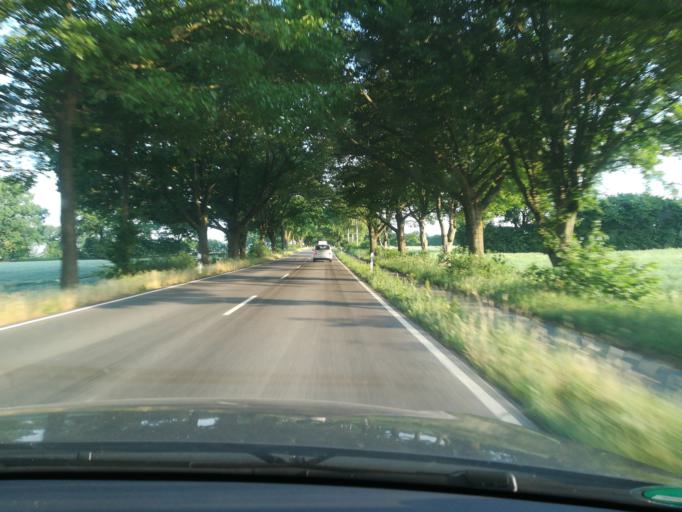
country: DE
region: Schleswig-Holstein
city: Hoisdorf
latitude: 53.6262
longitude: 10.3257
